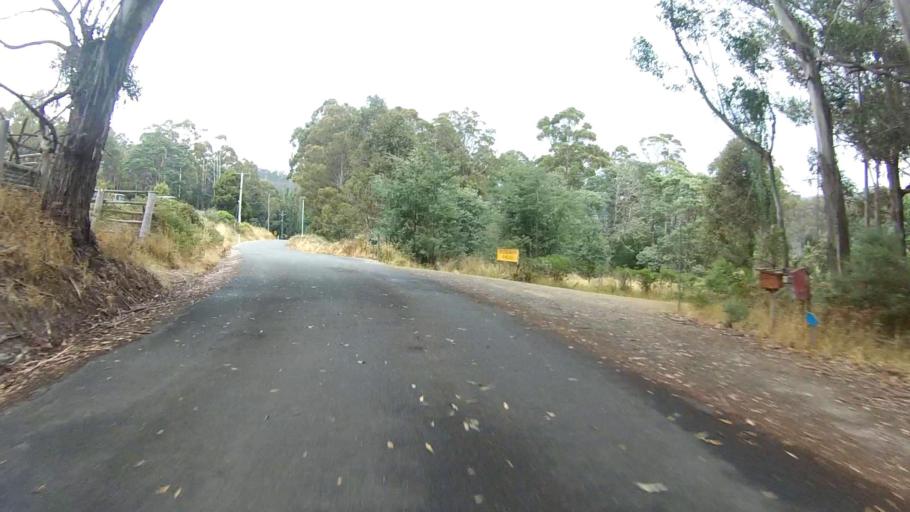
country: AU
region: Tasmania
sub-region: Huon Valley
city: Cygnet
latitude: -43.2344
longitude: 147.1570
